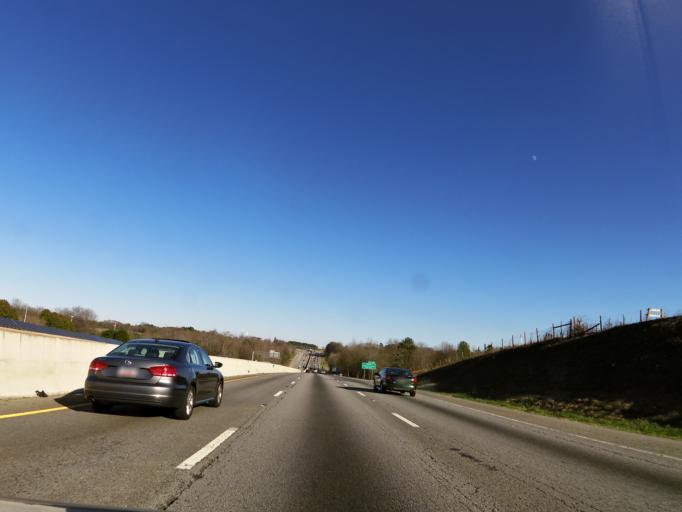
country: US
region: South Carolina
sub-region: Spartanburg County
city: Duncan
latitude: 34.8886
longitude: -82.1757
